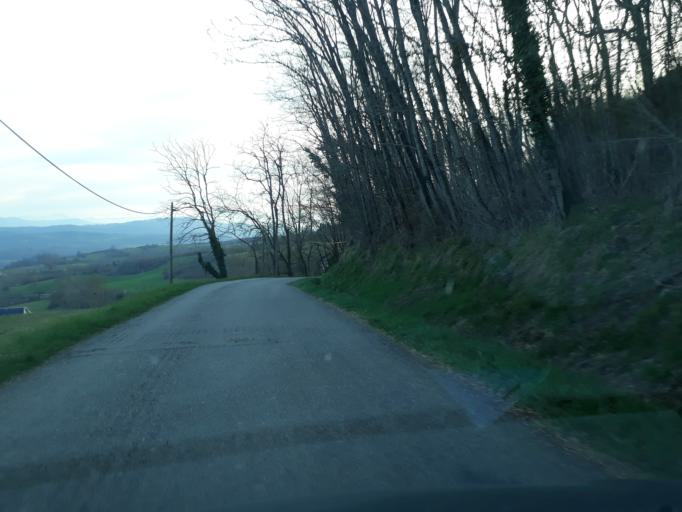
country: FR
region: Midi-Pyrenees
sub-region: Departement de la Haute-Garonne
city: Montesquieu-Volvestre
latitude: 43.1700
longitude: 1.3203
